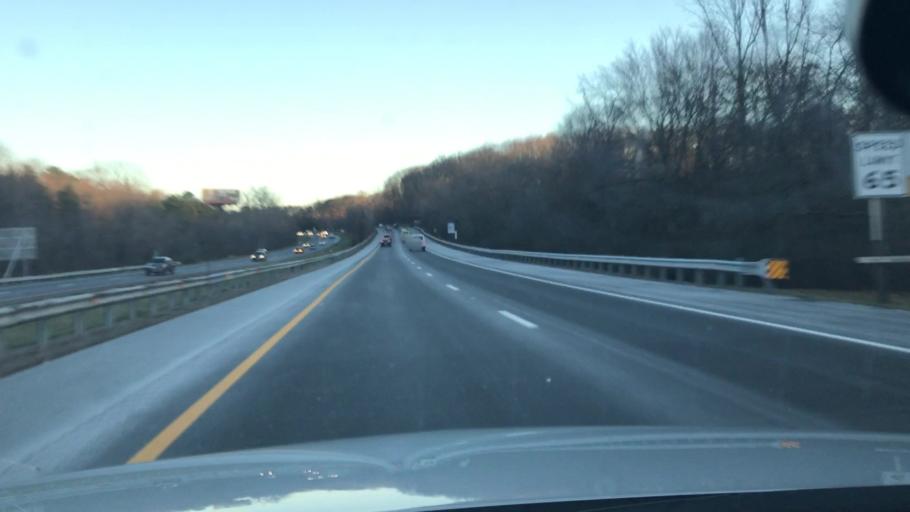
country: US
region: New Jersey
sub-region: Gloucester County
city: Turnersville
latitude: 39.7634
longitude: -75.0442
